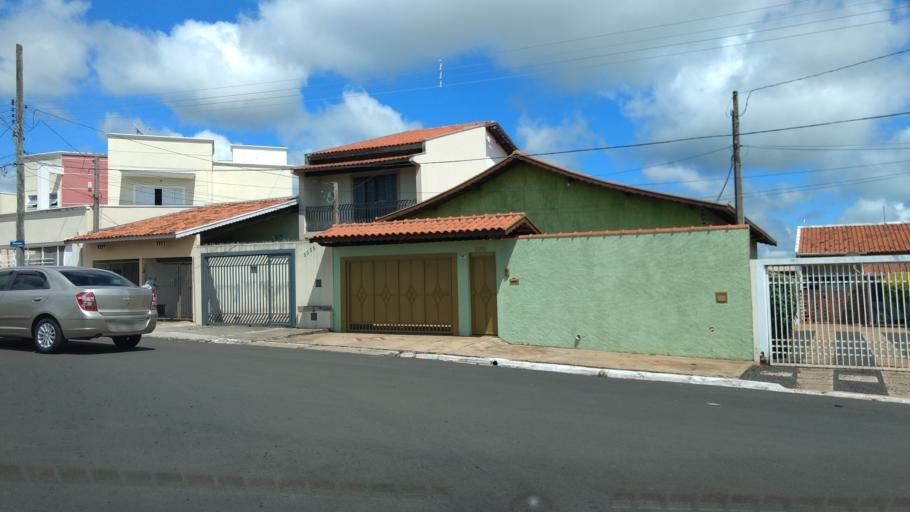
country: BR
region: Sao Paulo
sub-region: Botucatu
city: Botucatu
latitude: -22.8529
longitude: -48.4398
